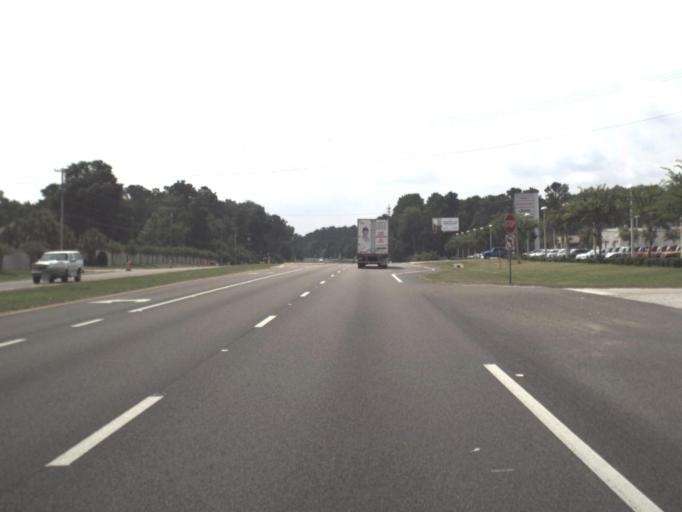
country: US
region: Florida
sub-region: Clay County
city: Green Cove Springs
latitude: 30.0163
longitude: -81.7023
